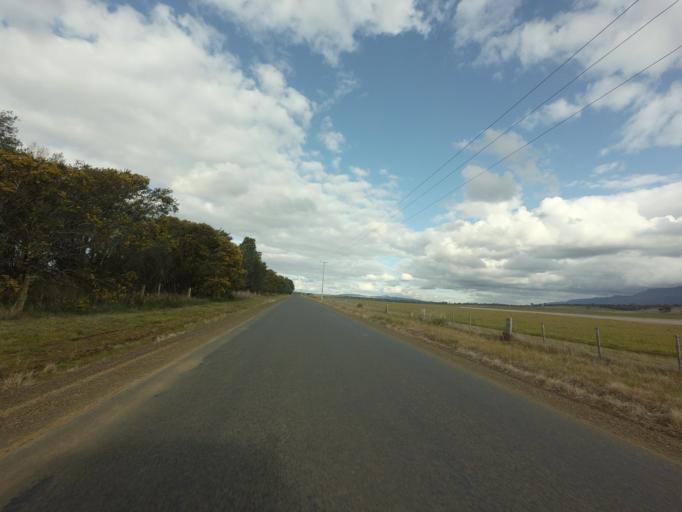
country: AU
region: Tasmania
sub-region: Northern Midlands
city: Longford
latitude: -41.8179
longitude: 147.1978
